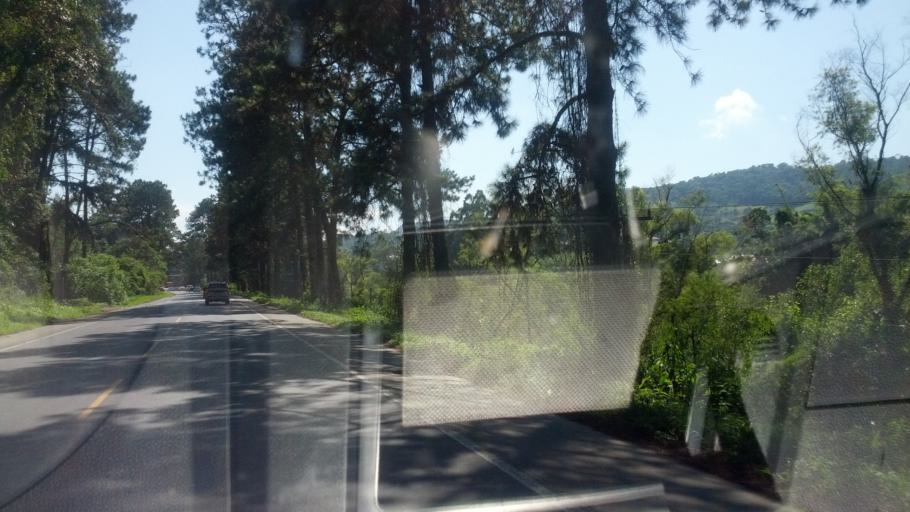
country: BR
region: Santa Catarina
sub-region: Rio Do Sul
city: Rio do Sul
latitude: -27.2343
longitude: -49.6755
